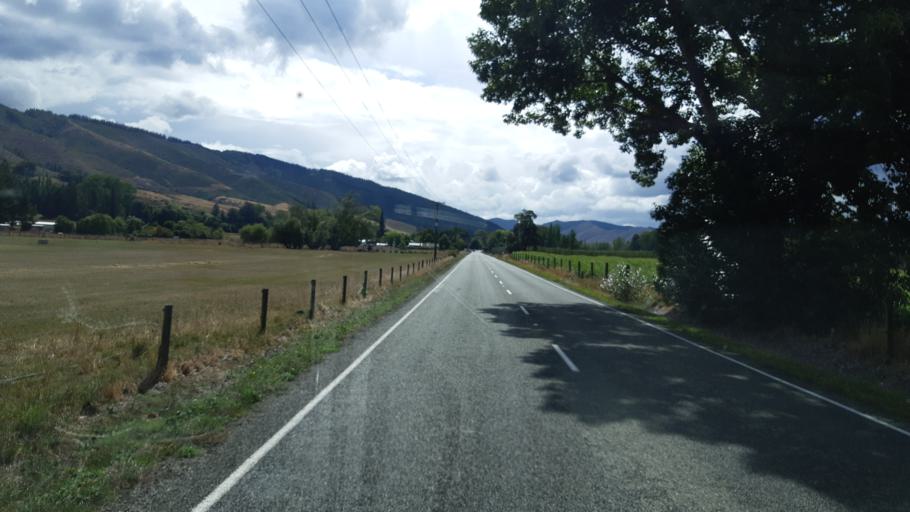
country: NZ
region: Tasman
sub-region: Tasman District
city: Wakefield
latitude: -41.4651
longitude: 172.8089
